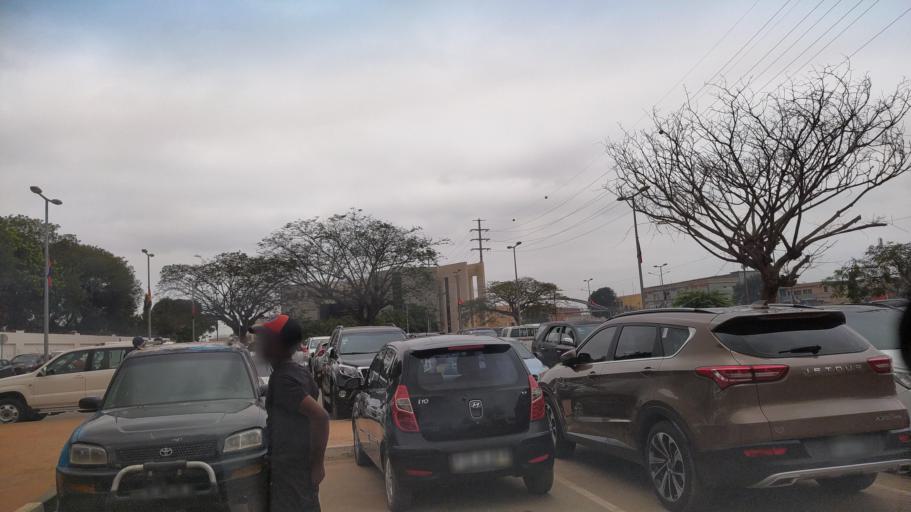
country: AO
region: Luanda
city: Luanda
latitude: -8.8398
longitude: 13.2651
